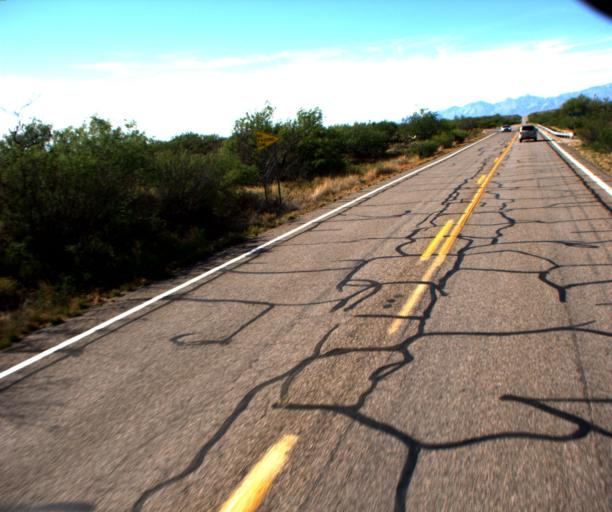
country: US
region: Arizona
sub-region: Pima County
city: Vail
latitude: 31.9617
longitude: -110.6714
